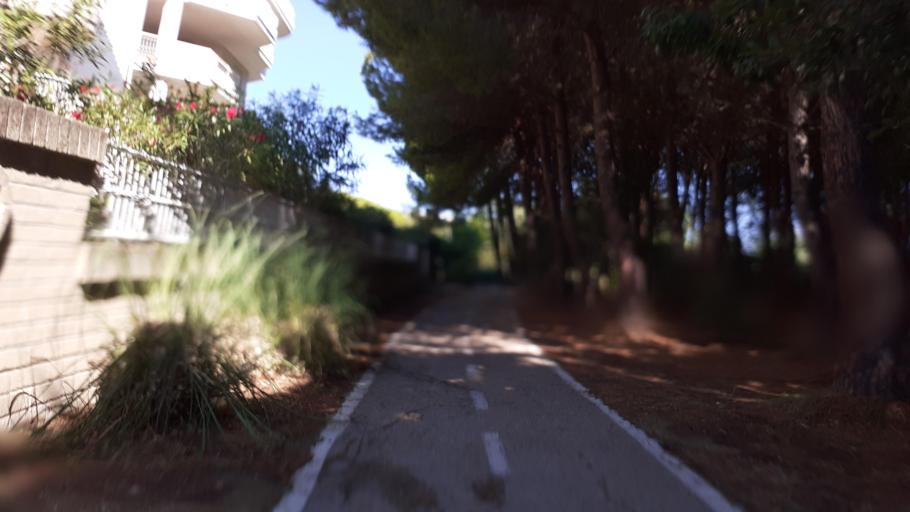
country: IT
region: Abruzzo
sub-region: Provincia di Chieti
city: Marina di Vasto
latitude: 42.0934
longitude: 14.7282
